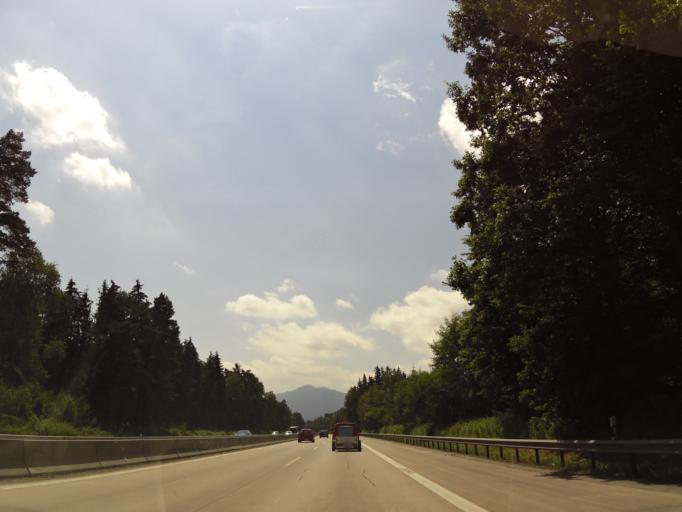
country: DE
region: Bavaria
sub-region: Upper Bavaria
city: Raubling
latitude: 47.7914
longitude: 12.0902
